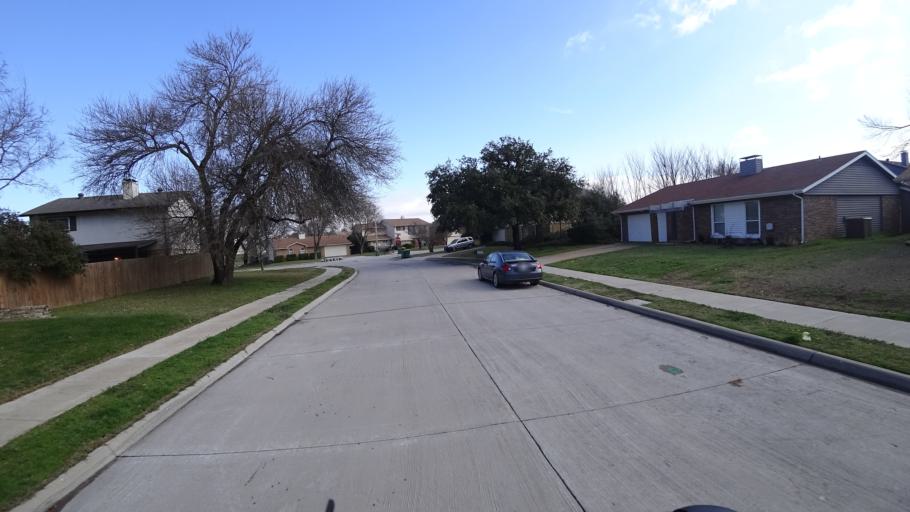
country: US
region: Texas
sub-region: Denton County
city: Lewisville
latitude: 33.0320
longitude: -97.0052
